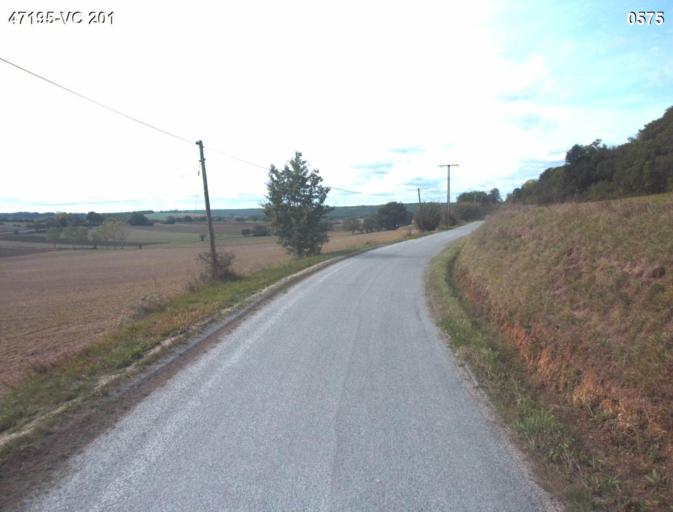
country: FR
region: Aquitaine
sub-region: Departement du Lot-et-Garonne
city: Nerac
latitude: 44.1306
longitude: 0.3107
